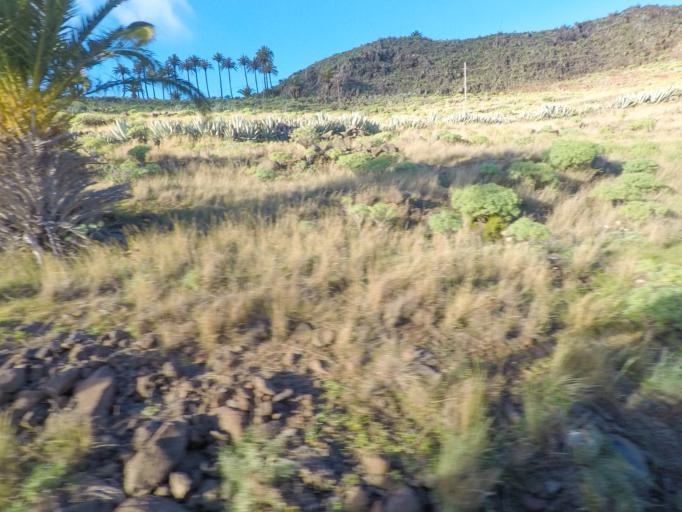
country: ES
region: Canary Islands
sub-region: Provincia de Santa Cruz de Tenerife
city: San Sebastian de la Gomera
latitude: 28.0982
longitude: -17.1632
